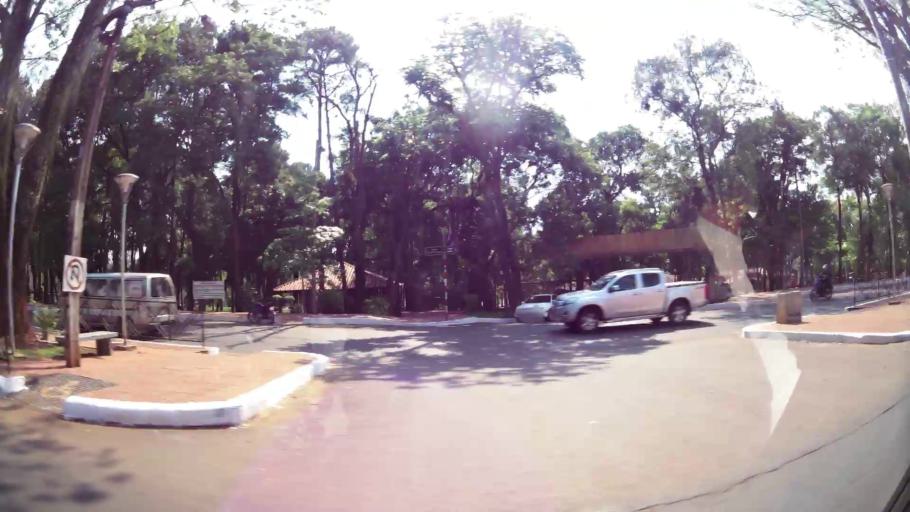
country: PY
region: Alto Parana
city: Ciudad del Este
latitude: -25.5124
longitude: -54.6152
